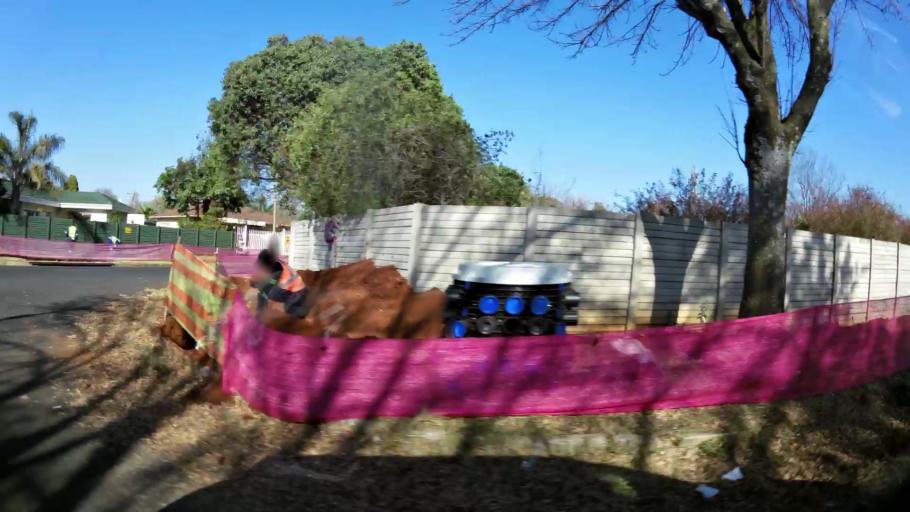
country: ZA
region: Gauteng
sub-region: Ekurhuleni Metropolitan Municipality
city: Benoni
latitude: -26.1550
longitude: 28.3104
